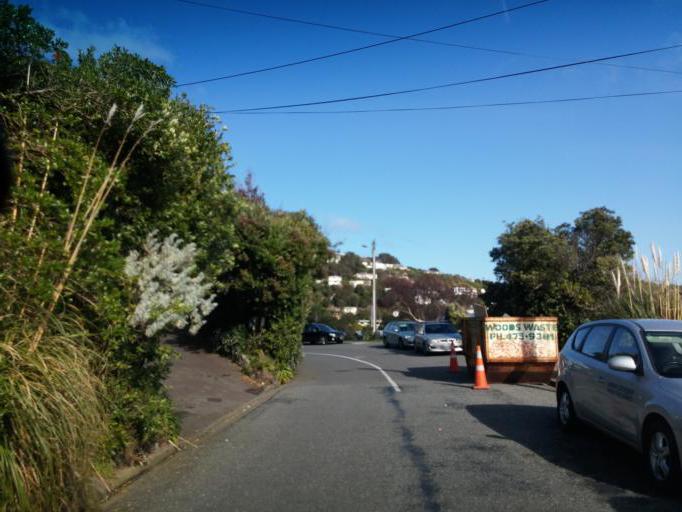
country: NZ
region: Wellington
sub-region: Wellington City
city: Wellington
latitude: -41.3228
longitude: 174.8258
